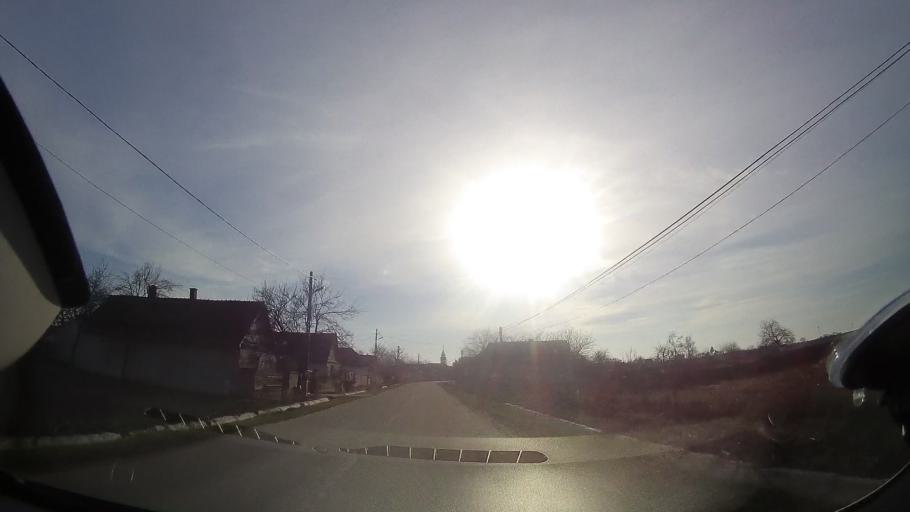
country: RO
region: Bihor
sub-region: Comuna Sarbi
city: Sarbi
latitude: 47.2102
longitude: 22.1318
